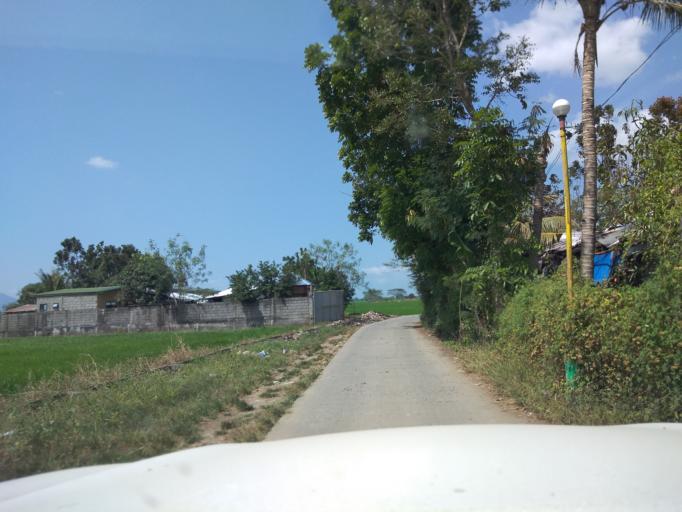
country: PH
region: Central Luzon
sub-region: Province of Pampanga
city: Bahay Pare
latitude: 15.0481
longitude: 120.8803
